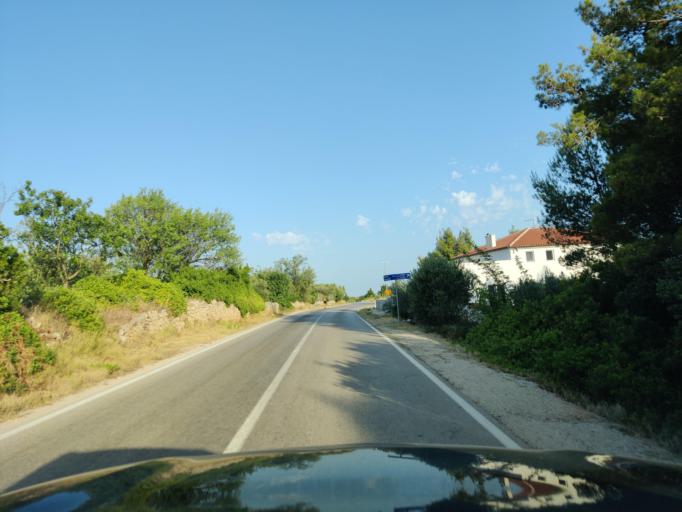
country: HR
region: Sibensko-Kniniska
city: Tribunj
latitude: 43.7649
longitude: 15.7366
